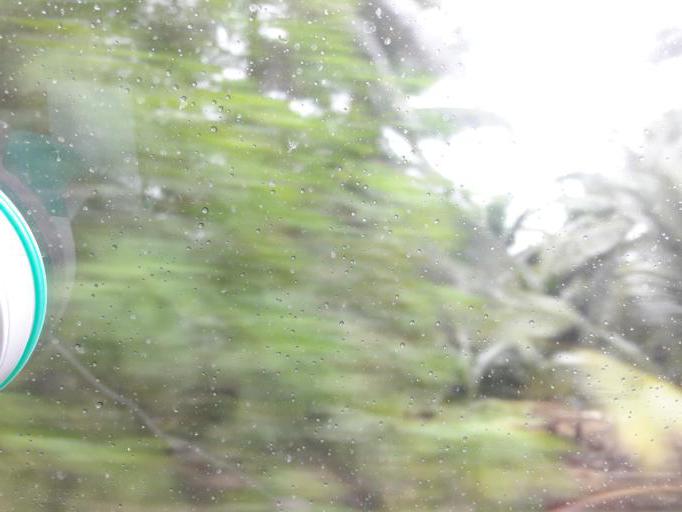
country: TH
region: Ratchaburi
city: Damnoen Saduak
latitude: 13.5114
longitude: 100.0165
